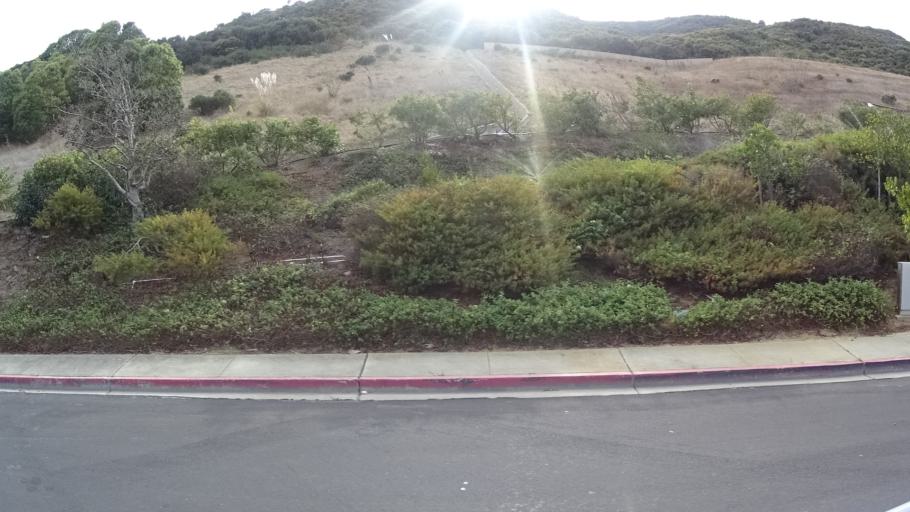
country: US
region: California
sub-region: San Mateo County
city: Brisbane
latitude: 37.7024
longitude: -122.4247
